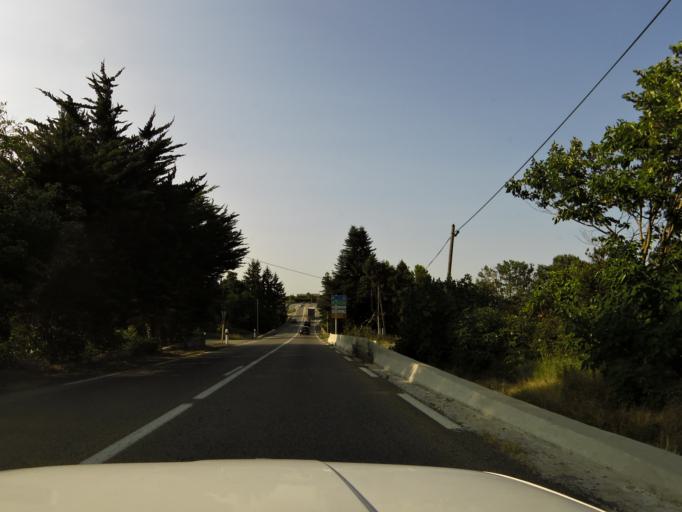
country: FR
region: Languedoc-Roussillon
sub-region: Departement du Gard
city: Saint-Alexandre
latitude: 44.2264
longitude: 4.6336
